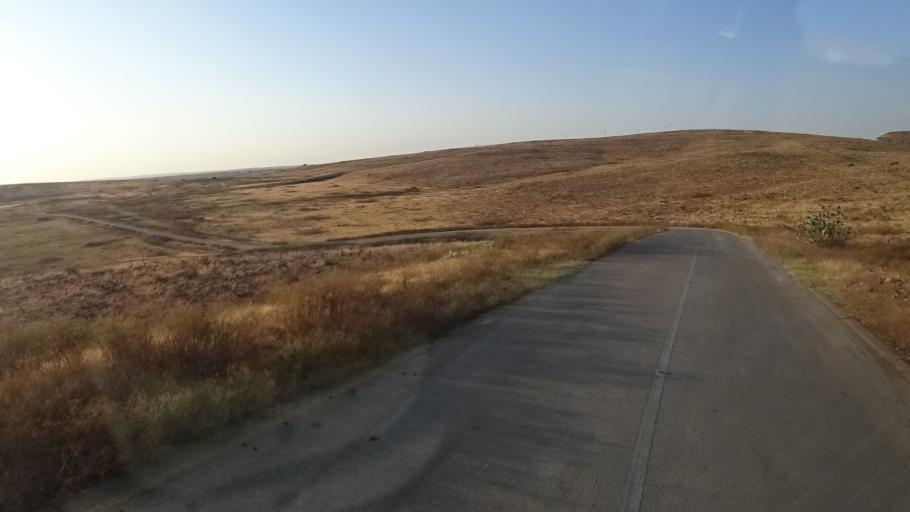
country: OM
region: Zufar
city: Salalah
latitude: 17.1540
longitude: 54.6220
